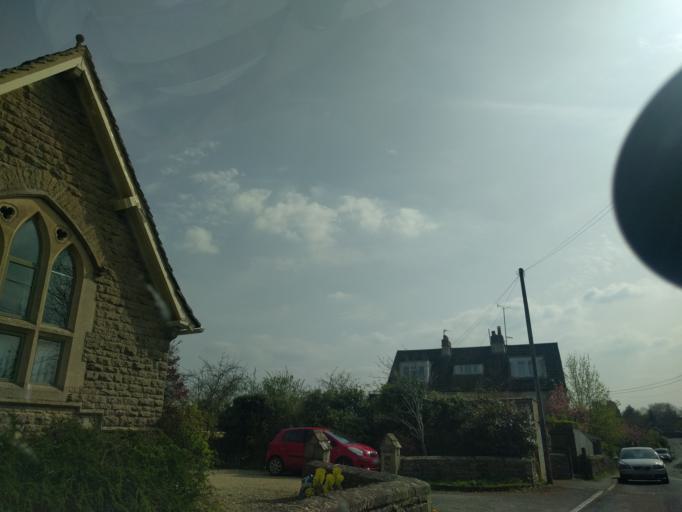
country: GB
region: England
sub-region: Wiltshire
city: Corsham
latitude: 51.4176
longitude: -2.1660
